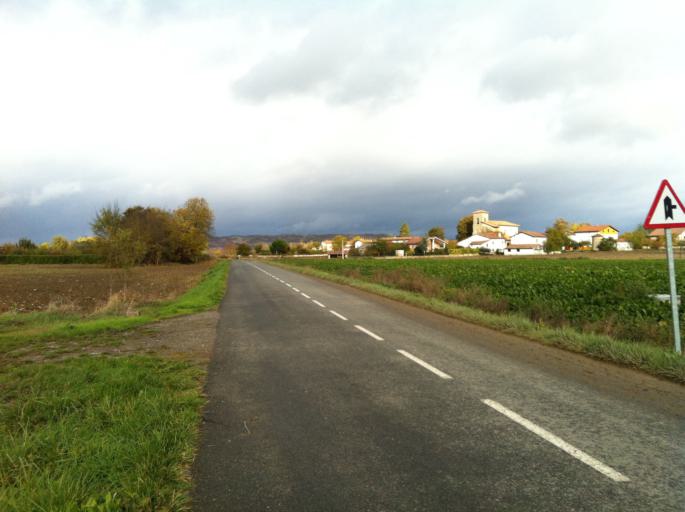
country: ES
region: Basque Country
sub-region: Provincia de Alava
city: Gasteiz / Vitoria
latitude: 42.8714
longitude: -2.7155
